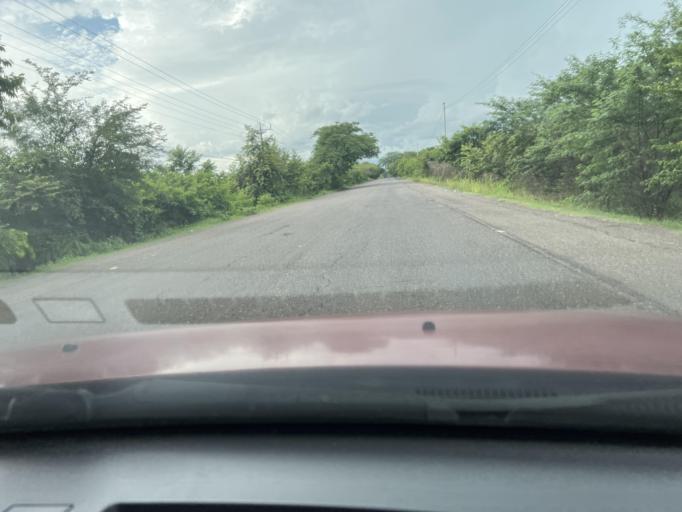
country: SV
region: La Union
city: San Alejo
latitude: 13.4187
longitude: -87.8872
